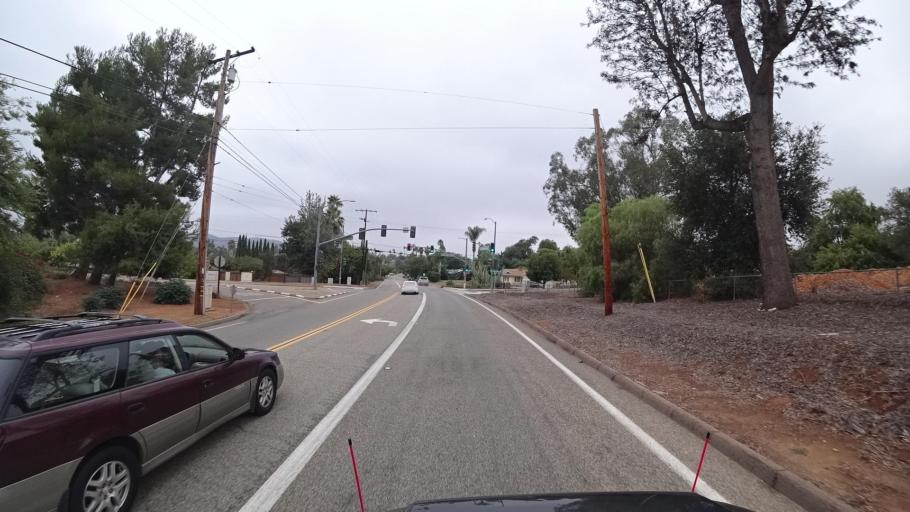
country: US
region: California
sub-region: San Diego County
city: Escondido
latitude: 33.0764
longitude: -117.0946
